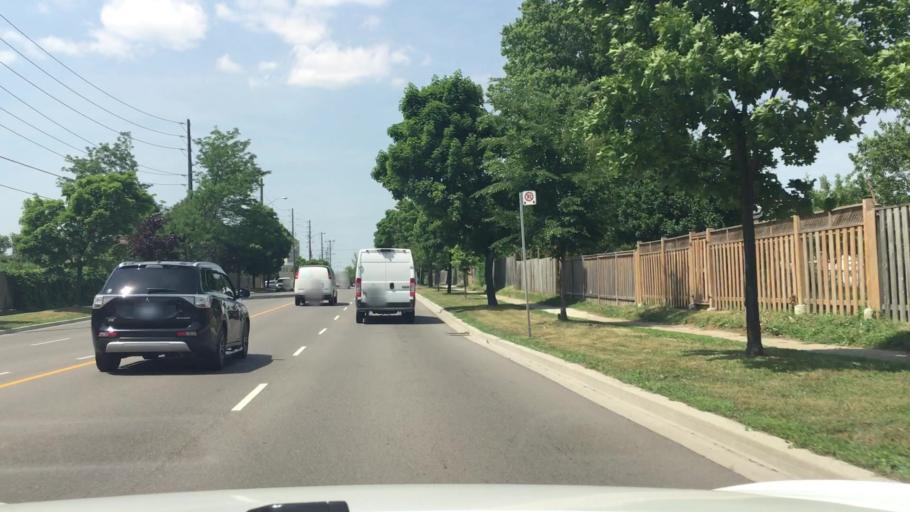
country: CA
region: Ontario
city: Scarborough
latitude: 43.7777
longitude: -79.2964
